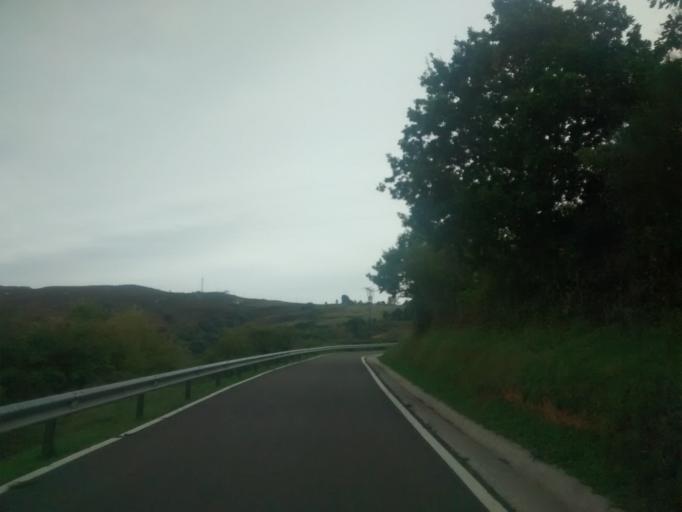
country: ES
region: Cantabria
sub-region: Provincia de Cantabria
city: San Miguel de Aguayo
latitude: 42.9703
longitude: -4.0463
